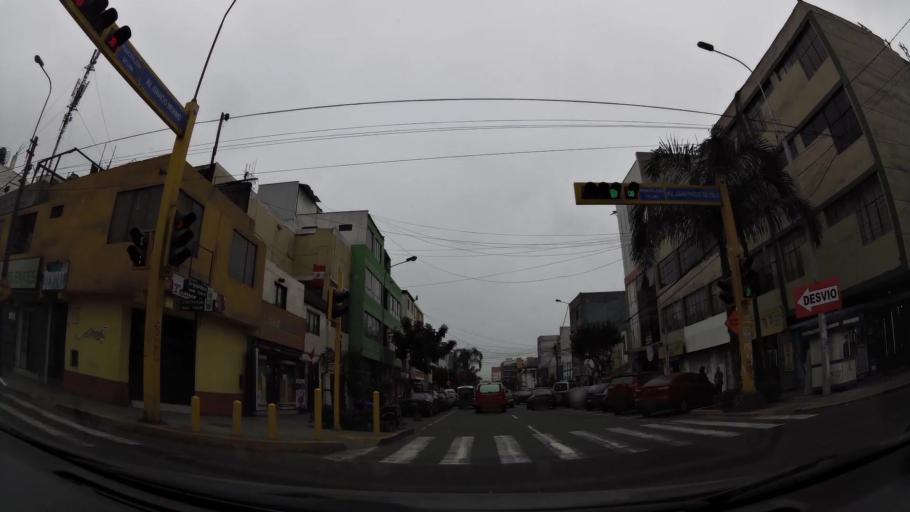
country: PE
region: Lima
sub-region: Lima
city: San Isidro
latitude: -12.0833
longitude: -77.0326
